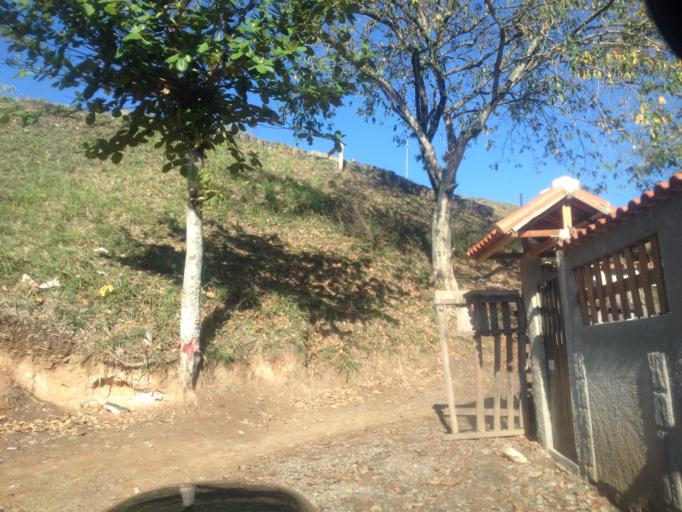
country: BR
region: Rio de Janeiro
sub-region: Porto Real
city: Porto Real
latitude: -22.4491
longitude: -44.3066
